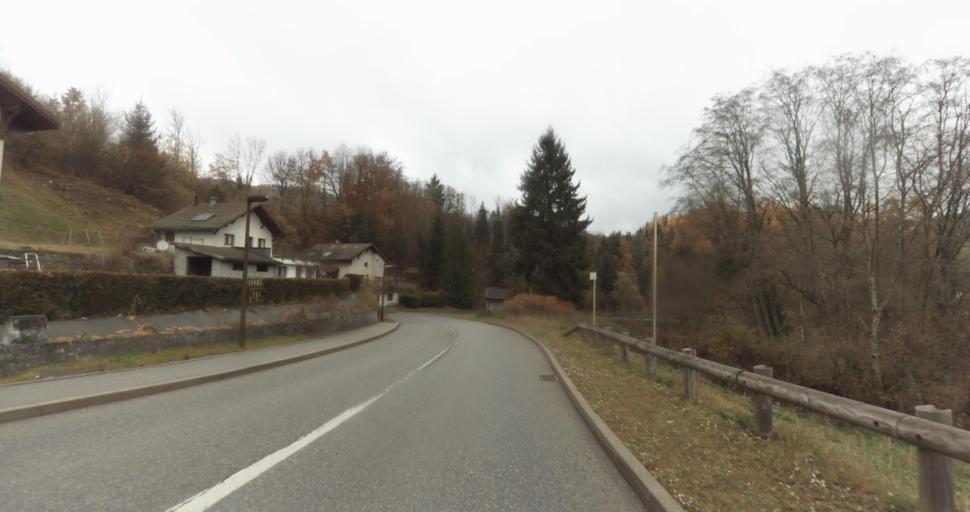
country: FR
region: Rhone-Alpes
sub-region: Departement de la Haute-Savoie
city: Thorens-Glieres
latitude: 45.9975
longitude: 6.2537
